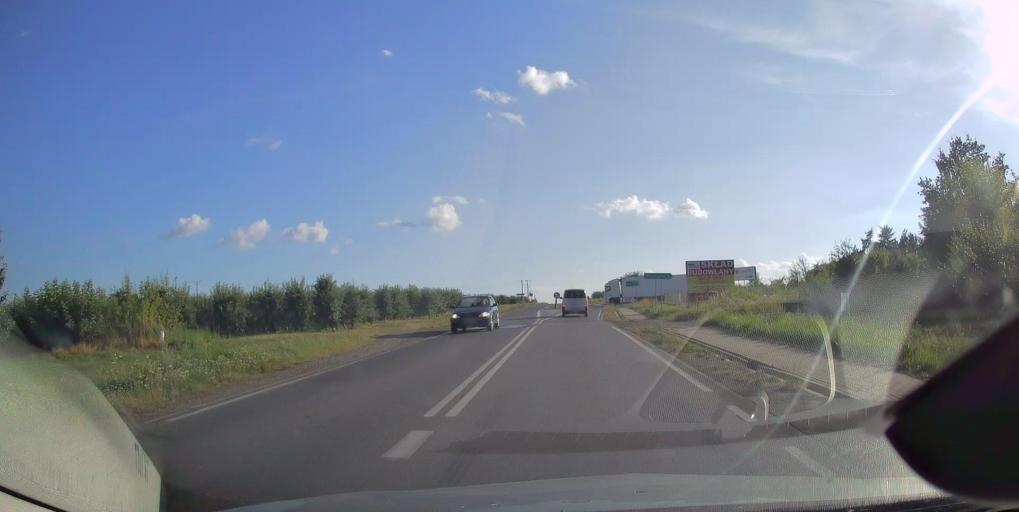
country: PL
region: Masovian Voivodeship
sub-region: Powiat grojecki
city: Belsk Duzy
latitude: 51.8410
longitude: 20.8289
